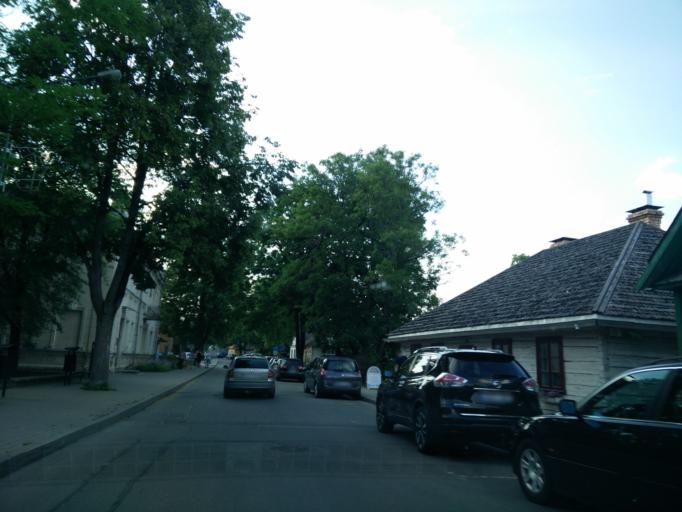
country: LT
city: Trakai
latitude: 54.6456
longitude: 24.9352
